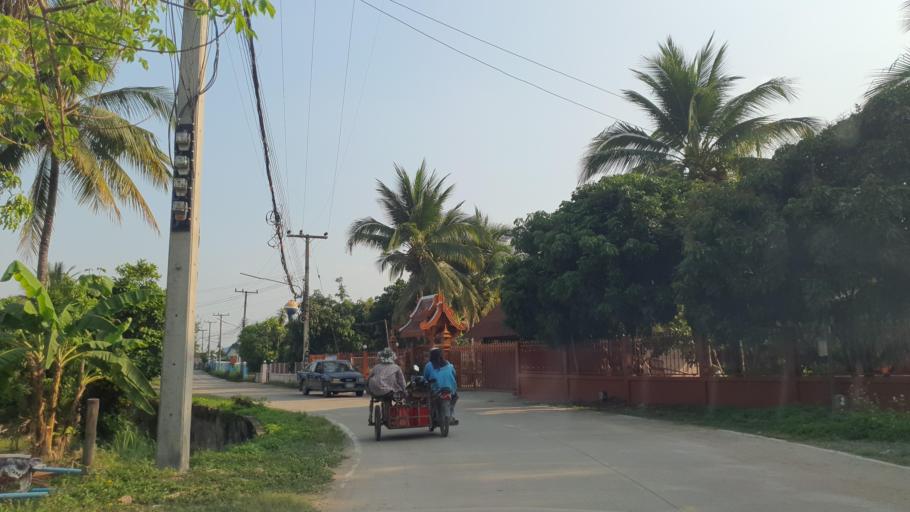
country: TH
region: Chiang Mai
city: Mae Wang
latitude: 18.6622
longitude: 98.8188
